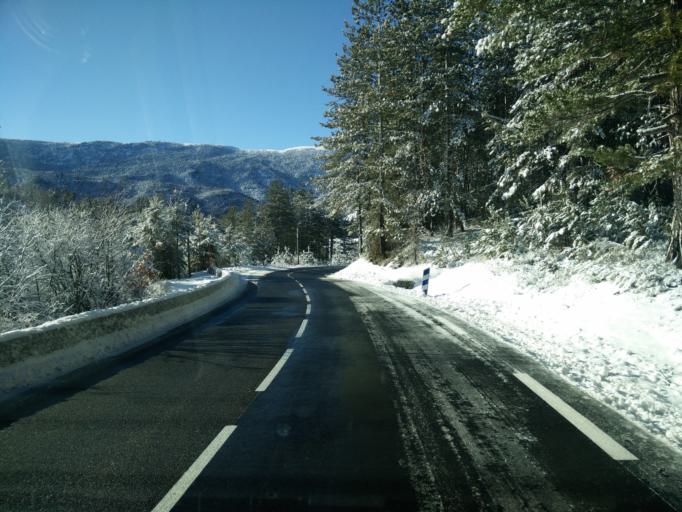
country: FR
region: Provence-Alpes-Cote d'Azur
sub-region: Departement des Alpes-de-Haute-Provence
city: Annot
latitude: 43.9181
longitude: 6.6115
